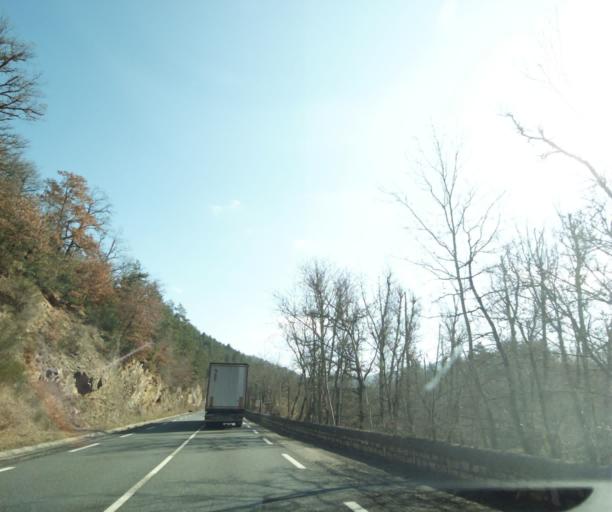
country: FR
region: Languedoc-Roussillon
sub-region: Departement de la Lozere
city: Chirac
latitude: 44.4922
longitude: 3.2635
